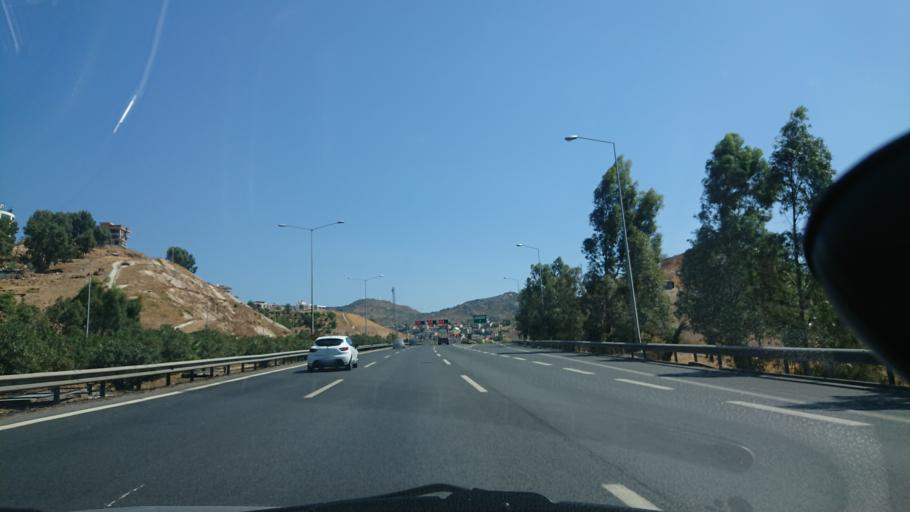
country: TR
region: Izmir
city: Karsiyaka
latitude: 38.4862
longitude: 27.1275
